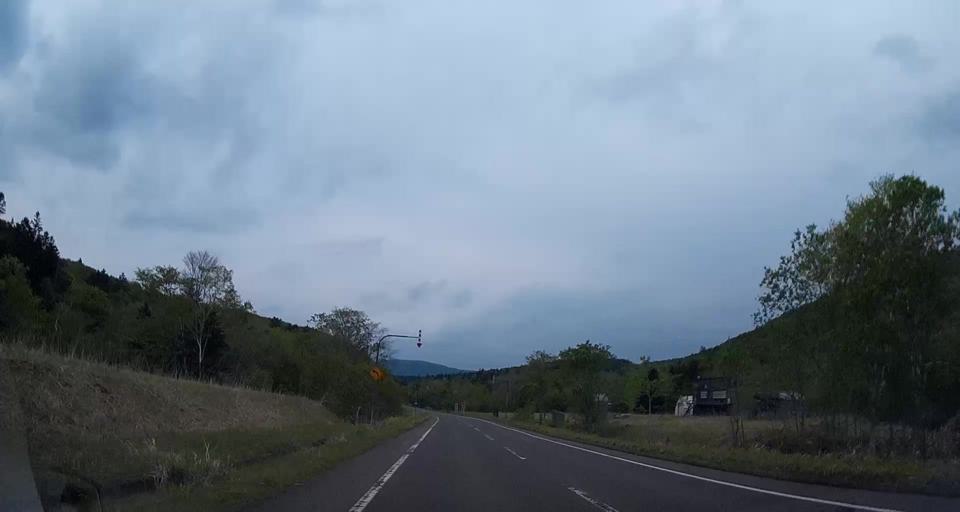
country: JP
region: Hokkaido
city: Shiraoi
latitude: 42.6768
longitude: 141.1435
